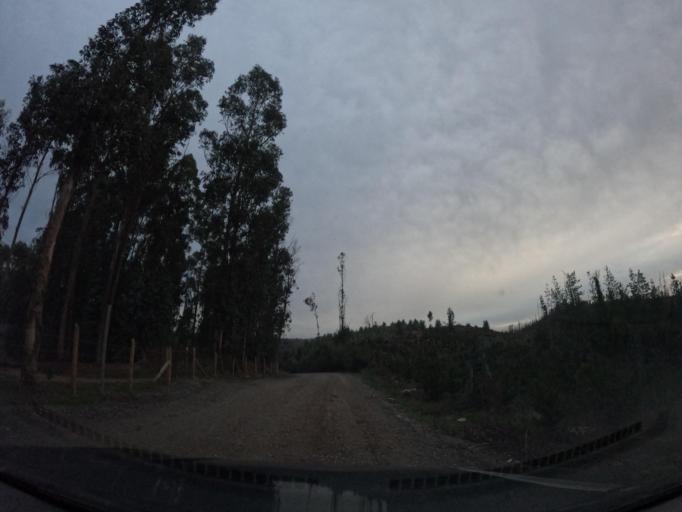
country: CL
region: Biobio
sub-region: Provincia de Concepcion
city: Chiguayante
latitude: -37.0101
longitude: -72.8951
